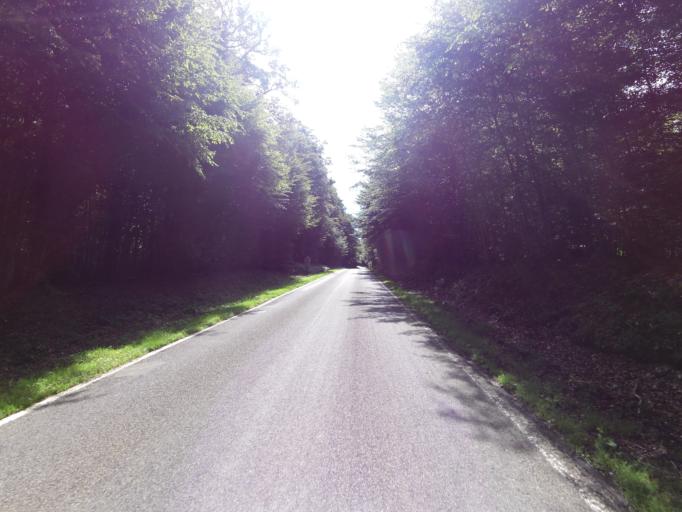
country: BE
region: Wallonia
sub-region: Province du Luxembourg
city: Nassogne
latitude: 50.0811
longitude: 5.3426
